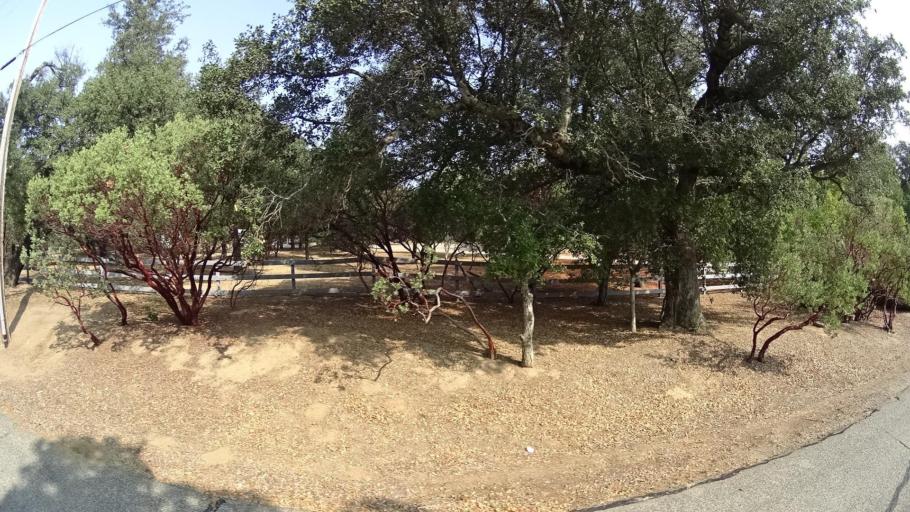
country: US
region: California
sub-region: San Diego County
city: Julian
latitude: 33.0956
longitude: -116.6554
